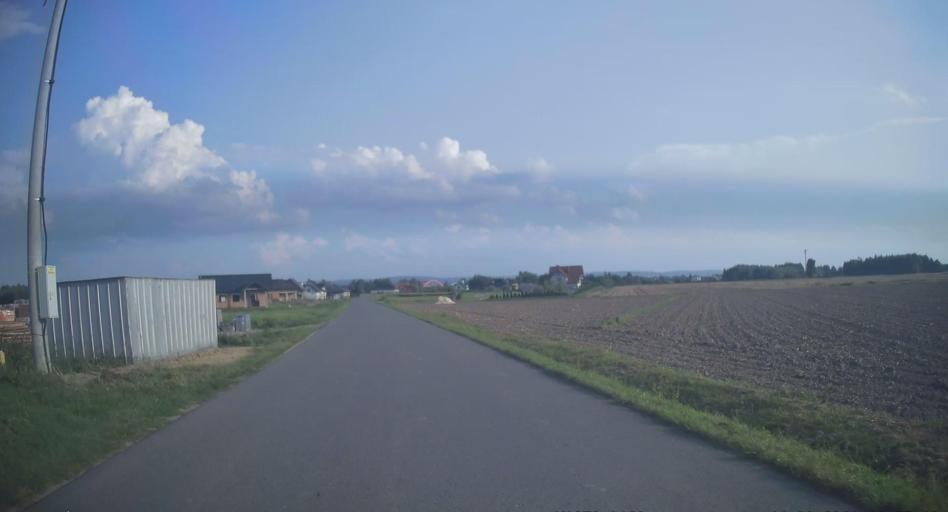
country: PL
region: Subcarpathian Voivodeship
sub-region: Powiat debicki
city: Zyrakow
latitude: 50.0873
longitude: 21.3813
